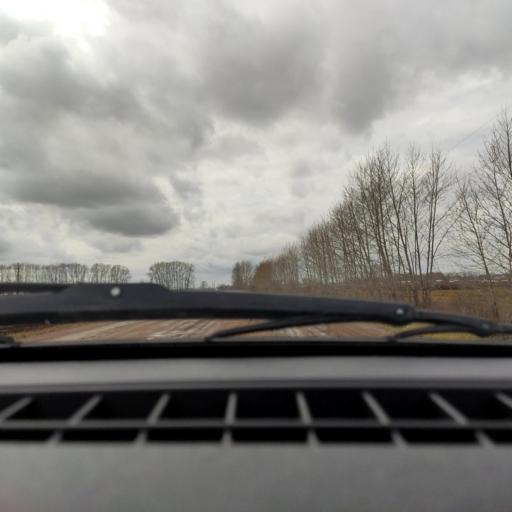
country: RU
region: Bashkortostan
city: Asanovo
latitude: 54.9596
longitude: 55.5744
